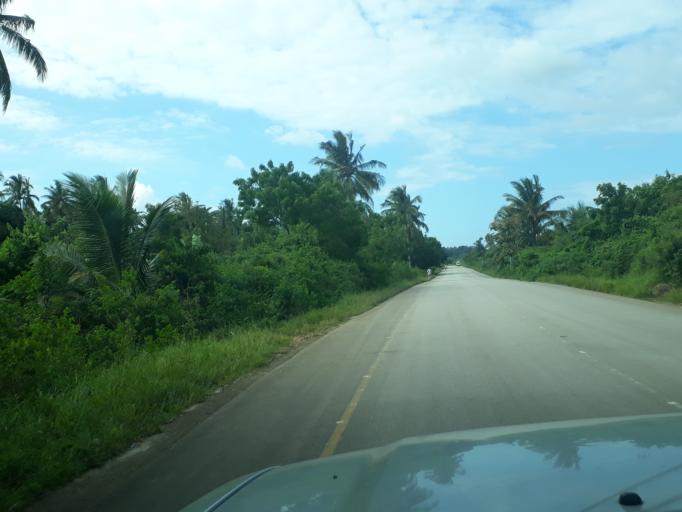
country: TZ
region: Zanzibar North
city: Kijini
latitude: -5.8401
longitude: 39.2847
